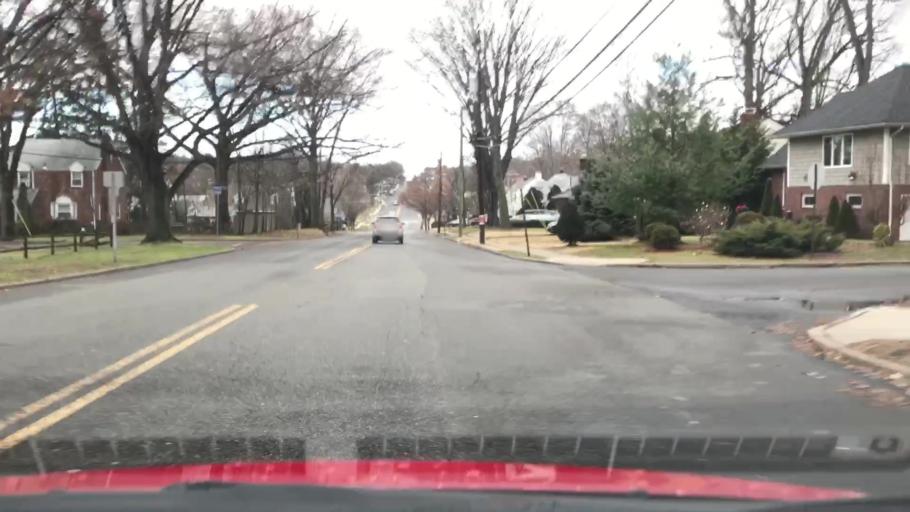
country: US
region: New Jersey
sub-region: Bergen County
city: Teaneck
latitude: 40.8833
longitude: -74.0039
